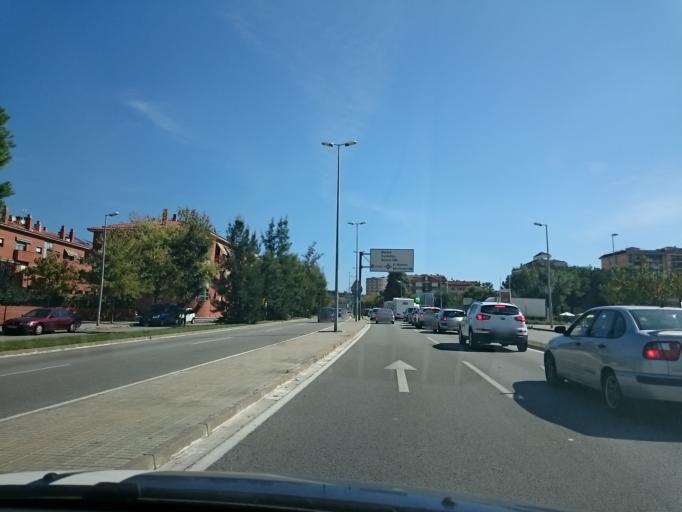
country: ES
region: Catalonia
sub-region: Provincia de Barcelona
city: Granollers
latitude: 41.5971
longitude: 2.2843
